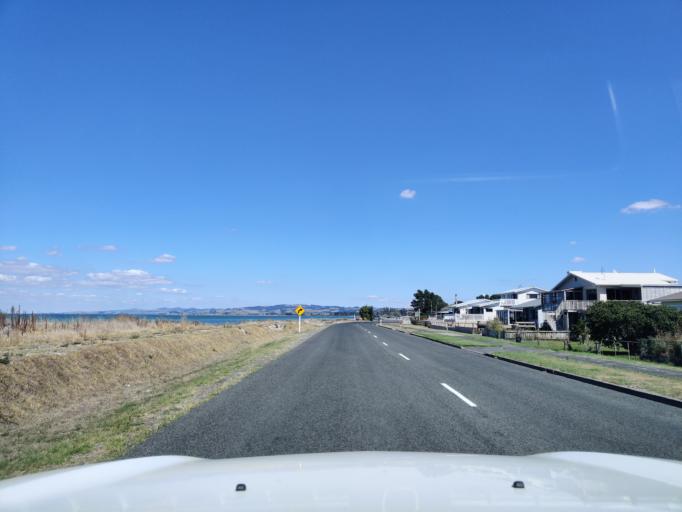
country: NZ
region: Waikato
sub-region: Thames-Coromandel District
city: Thames
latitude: -37.1077
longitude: 175.2991
